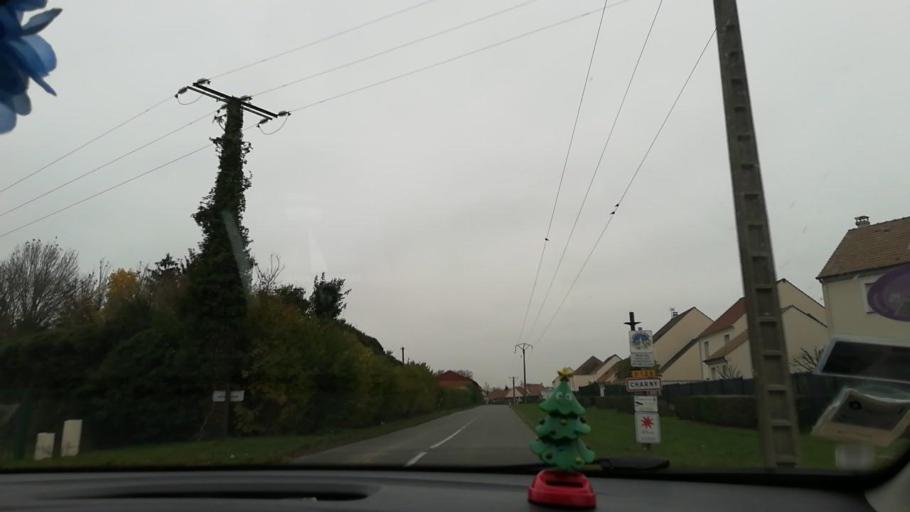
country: FR
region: Ile-de-France
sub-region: Departement de Seine-et-Marne
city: Charny
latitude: 48.9744
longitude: 2.7663
